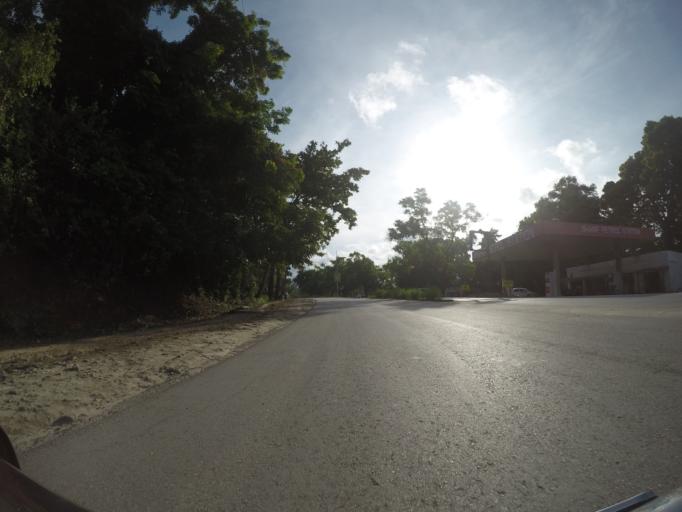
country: TZ
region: Pemba South
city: Chake Chake
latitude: -5.2376
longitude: 39.7746
